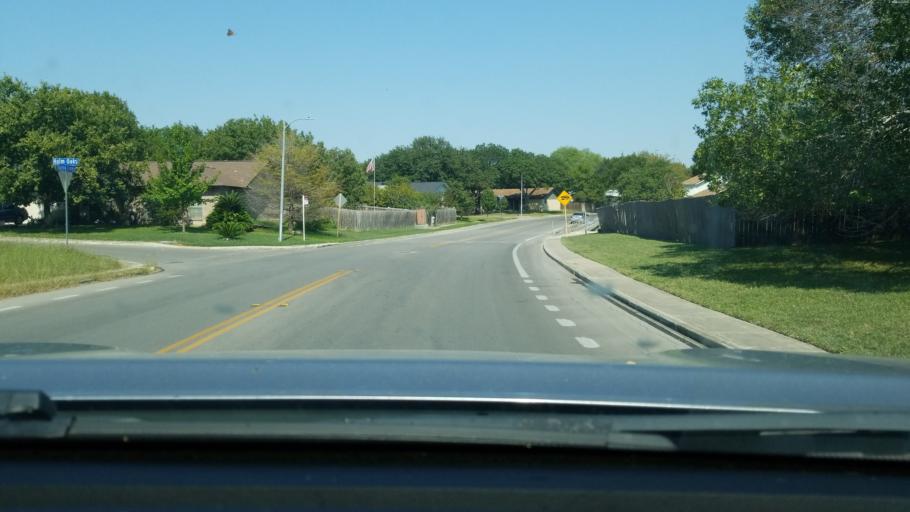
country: US
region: Texas
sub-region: Bexar County
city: Leon Valley
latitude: 29.5537
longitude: -98.6115
